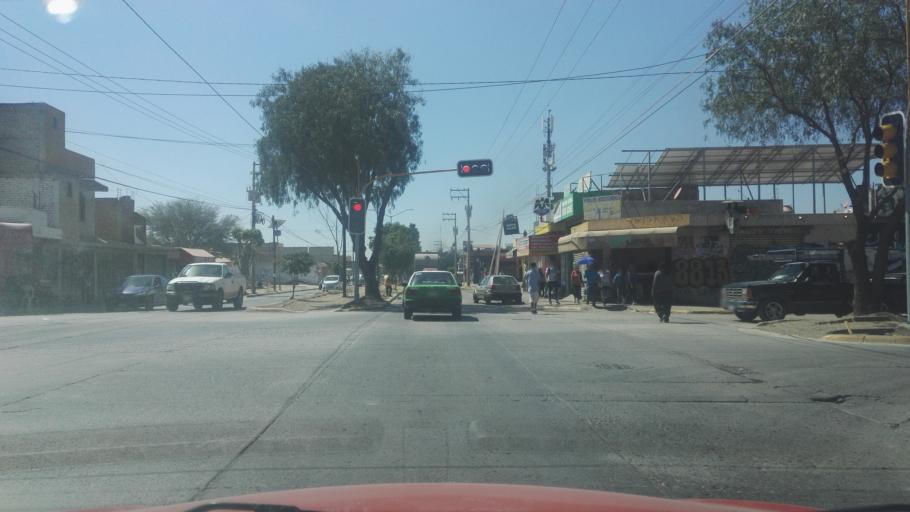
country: MX
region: Guanajuato
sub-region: Leon
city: Fraccionamiento Paraiso Real
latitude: 21.0973
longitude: -101.5894
